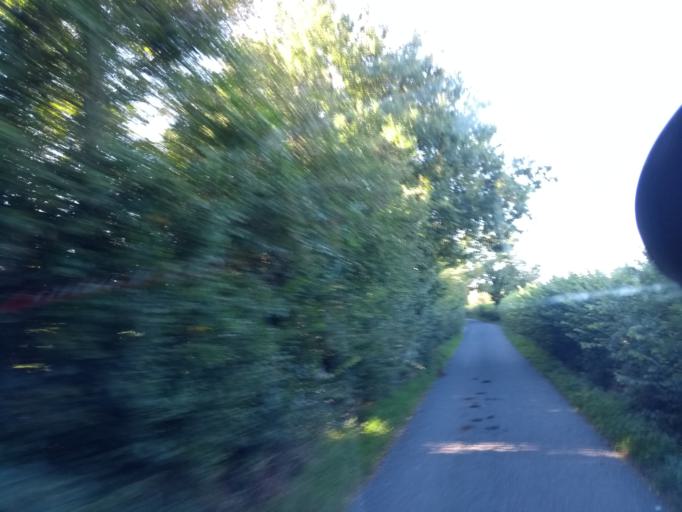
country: GB
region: England
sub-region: Somerset
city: Axbridge
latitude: 51.2578
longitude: -2.8640
